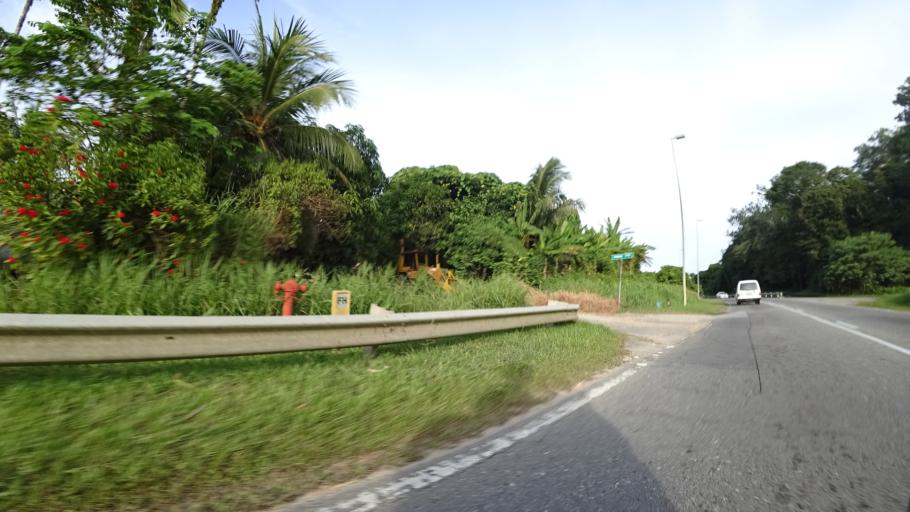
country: BN
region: Brunei and Muara
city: Bandar Seri Begawan
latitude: 4.8735
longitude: 114.8243
